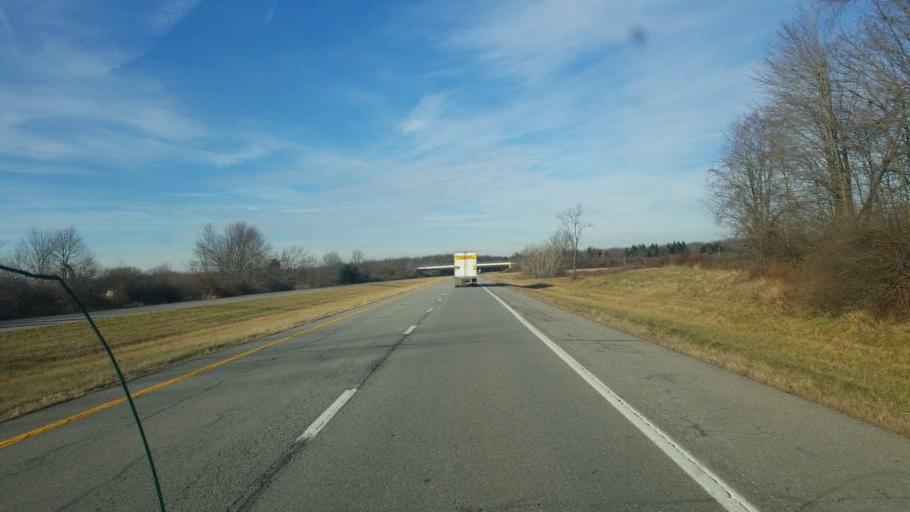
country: US
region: Ohio
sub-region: Trumbull County
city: Cortland
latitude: 41.4871
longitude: -80.7124
